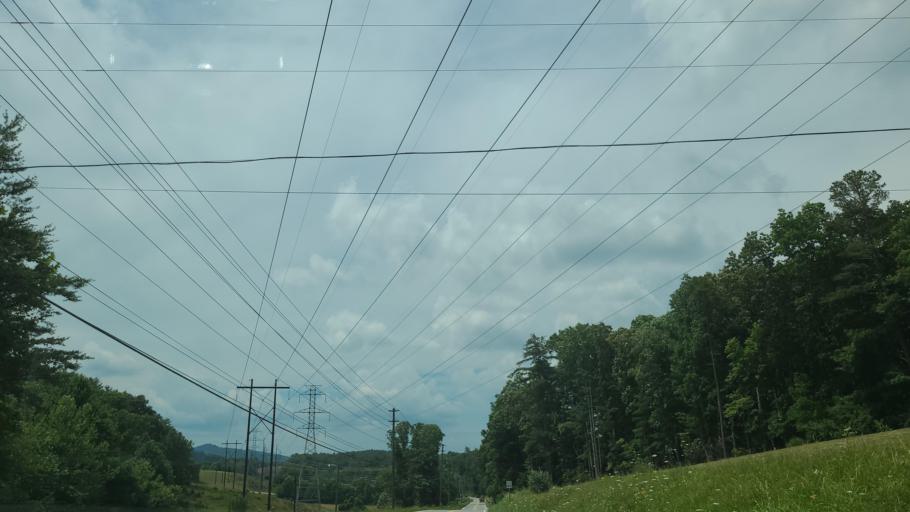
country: US
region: North Carolina
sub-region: Buncombe County
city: Avery Creek
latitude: 35.4847
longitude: -82.5705
